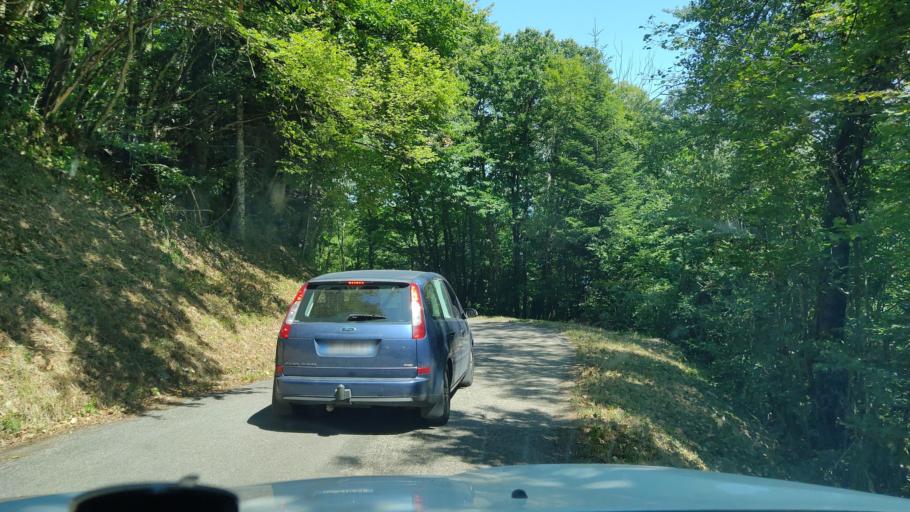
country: FR
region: Rhone-Alpes
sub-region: Departement de la Savoie
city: Le Bourget-du-Lac
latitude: 45.6499
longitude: 5.8372
